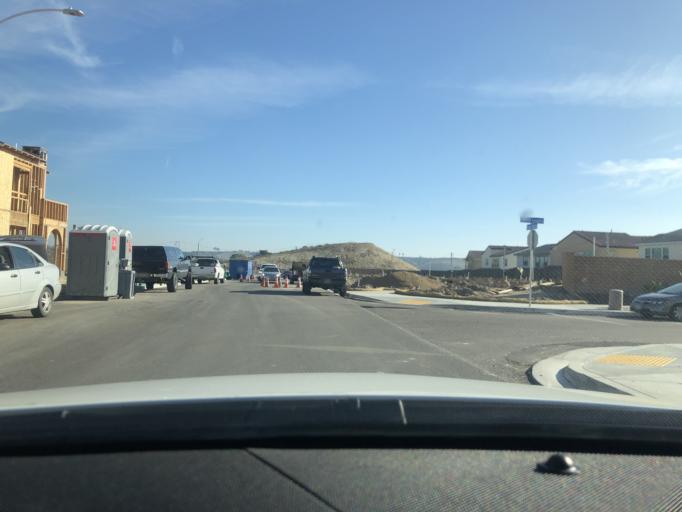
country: US
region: California
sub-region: San Diego County
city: Bonita
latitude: 32.5988
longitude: -116.9961
